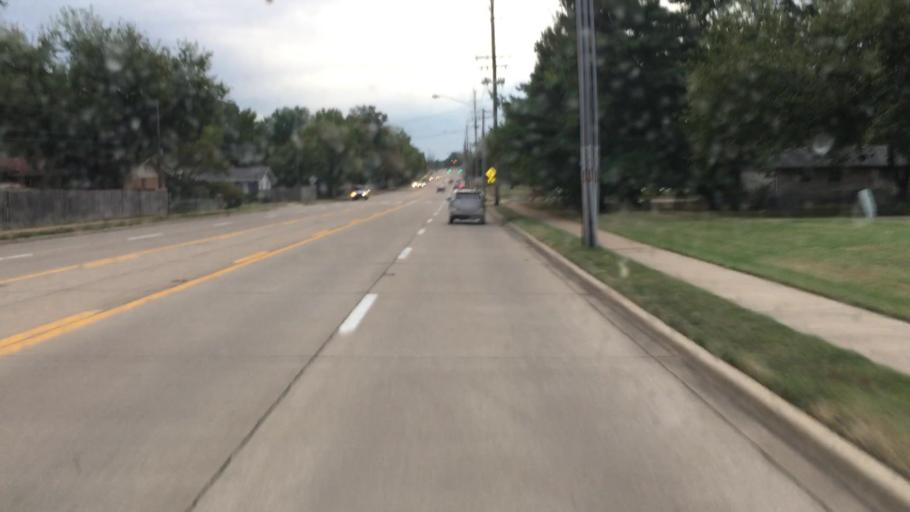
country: US
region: Missouri
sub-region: Saint Louis County
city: Florissant
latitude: 38.8240
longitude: -90.3376
